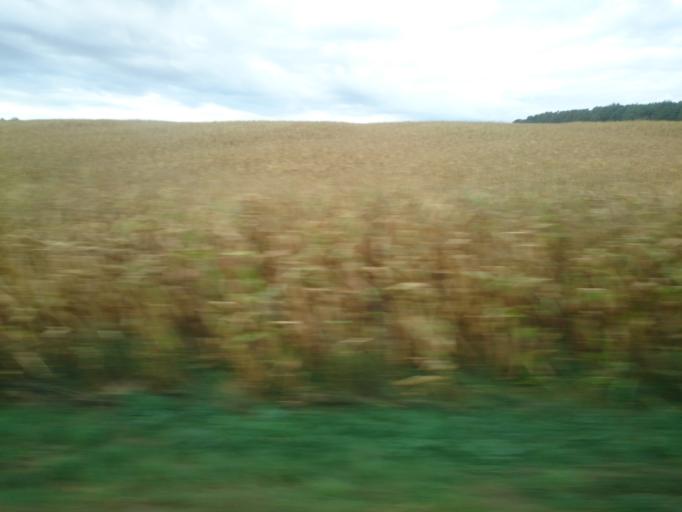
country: DE
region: Mecklenburg-Vorpommern
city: Jatznick
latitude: 53.5663
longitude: 13.9576
